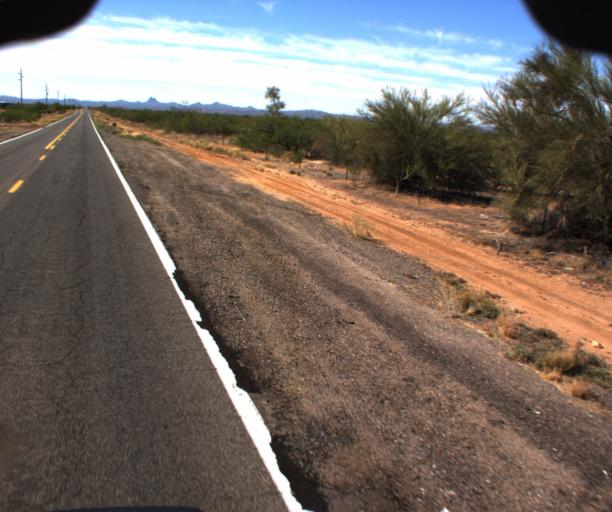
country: US
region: Arizona
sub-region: Yavapai County
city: Congress
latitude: 34.1180
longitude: -112.8353
